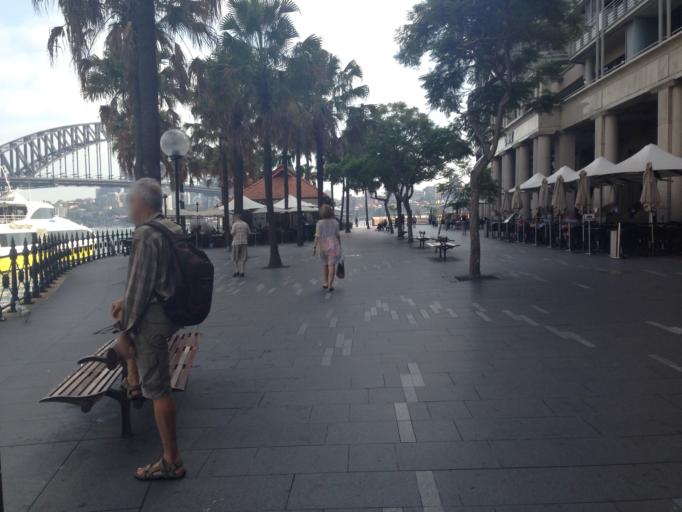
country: AU
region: New South Wales
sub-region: City of Sydney
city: Sydney
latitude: -33.8599
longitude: 151.2128
